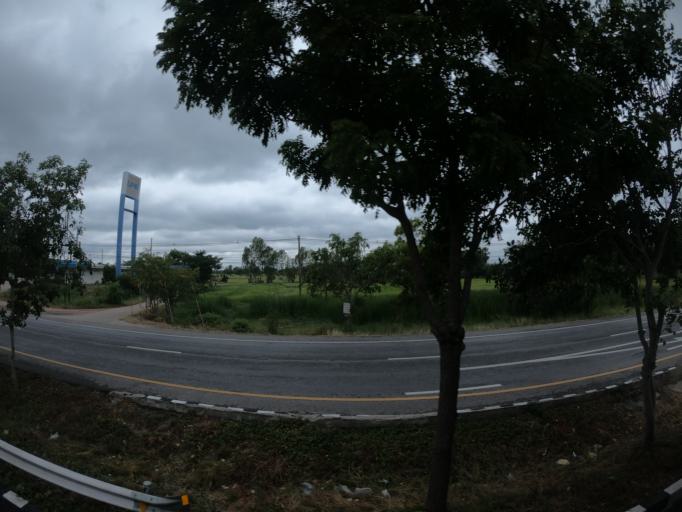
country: TH
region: Khon Kaen
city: Phon
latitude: 15.7545
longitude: 102.6044
